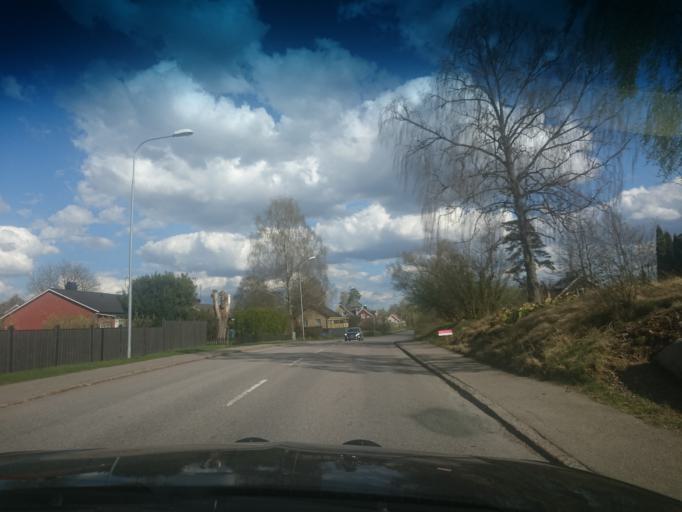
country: SE
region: Kronoberg
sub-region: Vaxjo Kommun
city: Braas
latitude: 57.1288
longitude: 15.1644
